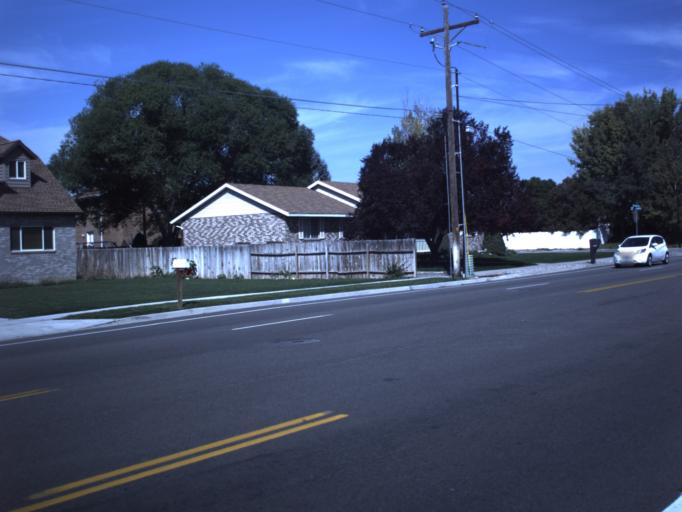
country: US
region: Utah
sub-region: Utah County
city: American Fork
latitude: 40.3774
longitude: -111.7690
